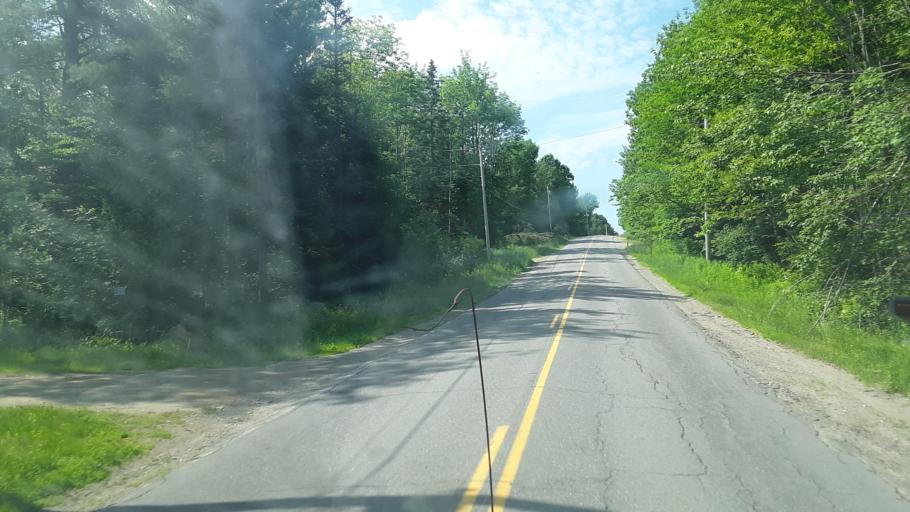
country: US
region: Maine
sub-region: Waldo County
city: Swanville
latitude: 44.5758
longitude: -68.9492
